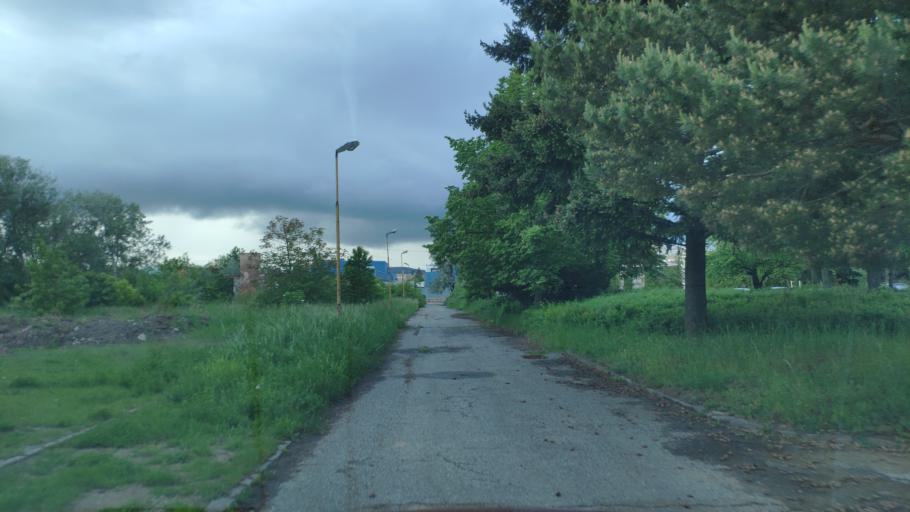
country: SK
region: Kosicky
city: Kosice
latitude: 48.7002
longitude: 21.2468
